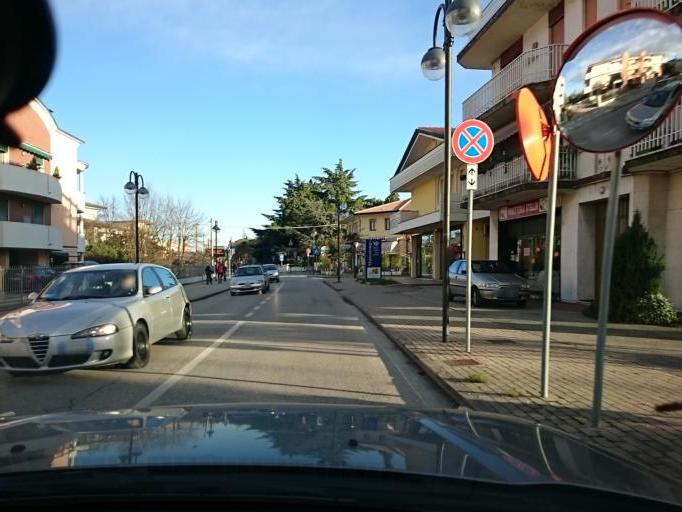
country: IT
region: Veneto
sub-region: Provincia di Padova
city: Montegrotto Terme
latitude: 45.3262
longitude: 11.7980
